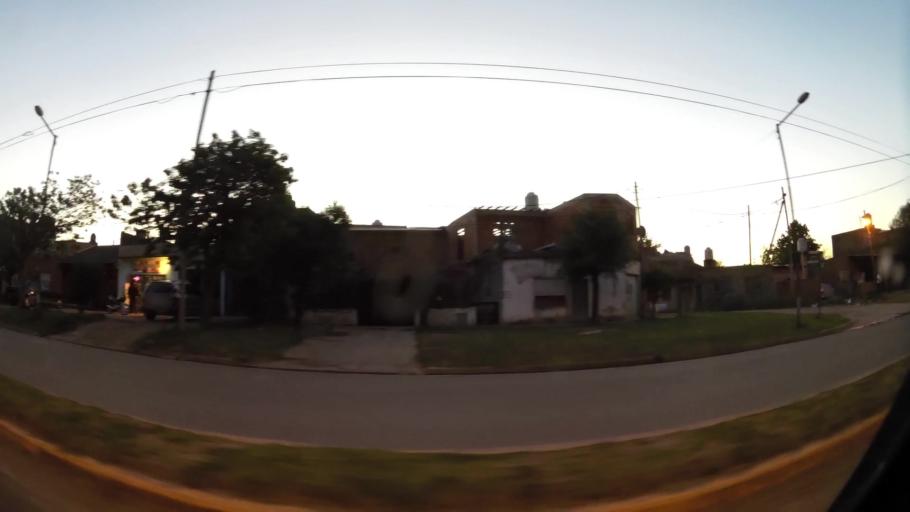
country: AR
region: Buenos Aires
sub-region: Partido de Almirante Brown
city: Adrogue
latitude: -34.7875
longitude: -58.3233
